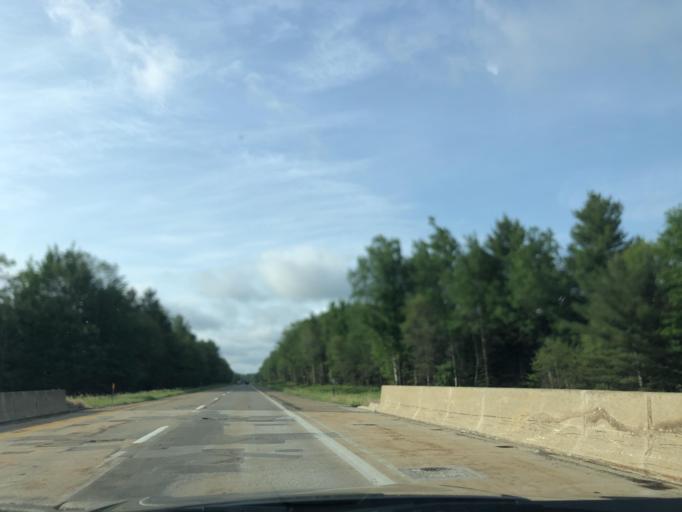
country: US
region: Michigan
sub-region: Roscommon County
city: Houghton Lake
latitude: 44.2098
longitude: -84.7957
